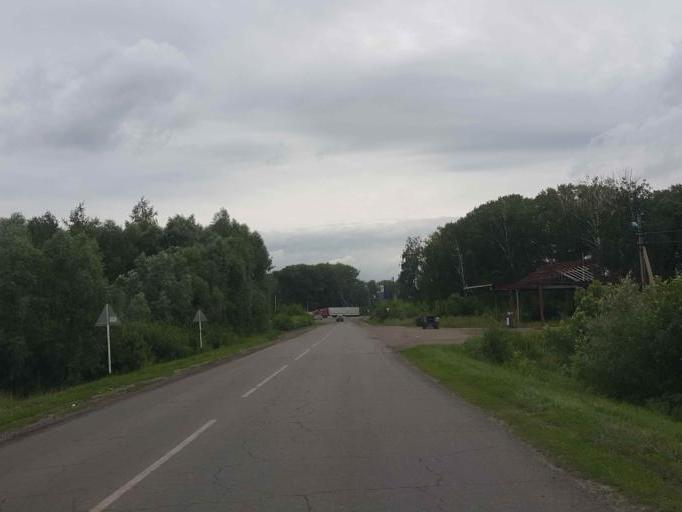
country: RU
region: Tambov
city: Zavoronezhskoye
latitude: 52.9542
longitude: 40.5760
